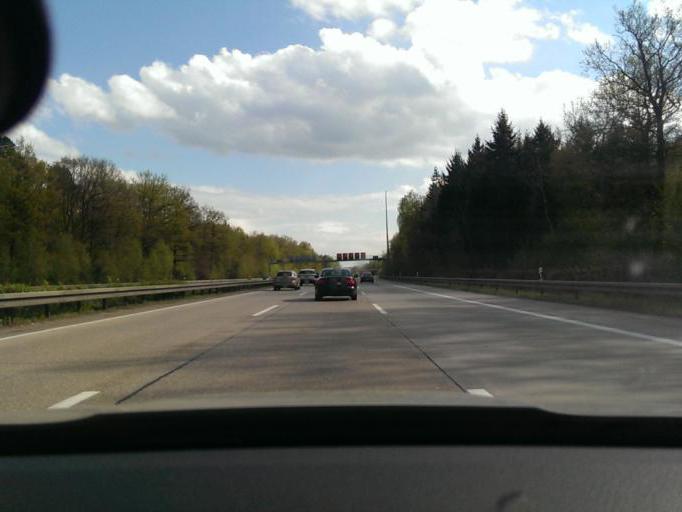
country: DE
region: Lower Saxony
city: Isernhagen Farster Bauerschaft
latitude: 52.4637
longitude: 9.8589
